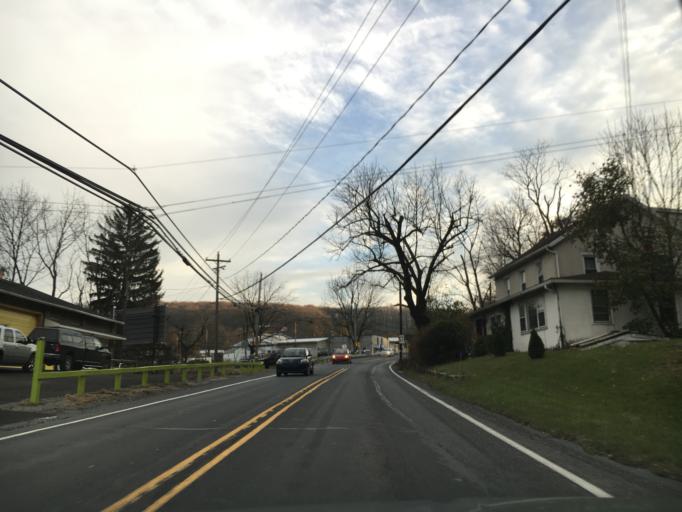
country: US
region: Pennsylvania
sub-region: Lehigh County
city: Slatington
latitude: 40.7254
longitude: -75.6169
